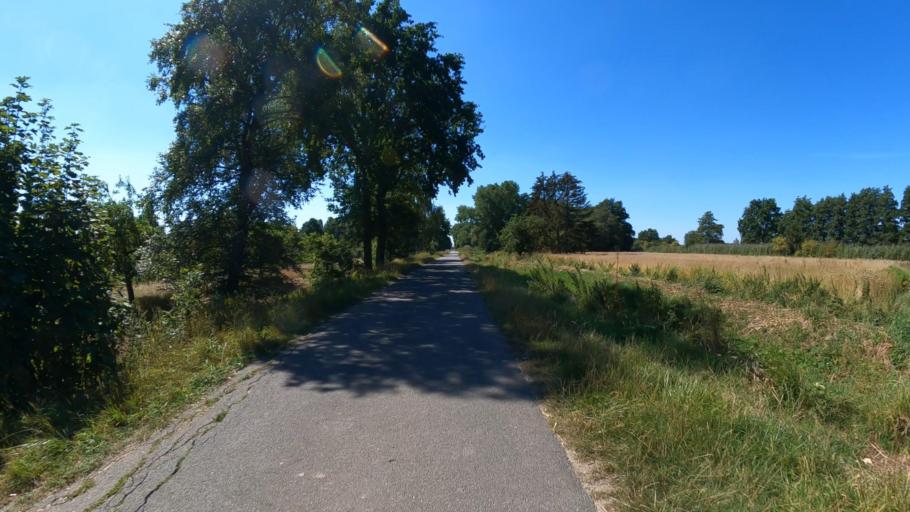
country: DE
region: Lower Saxony
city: Marschacht
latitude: 53.4132
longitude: 10.3451
